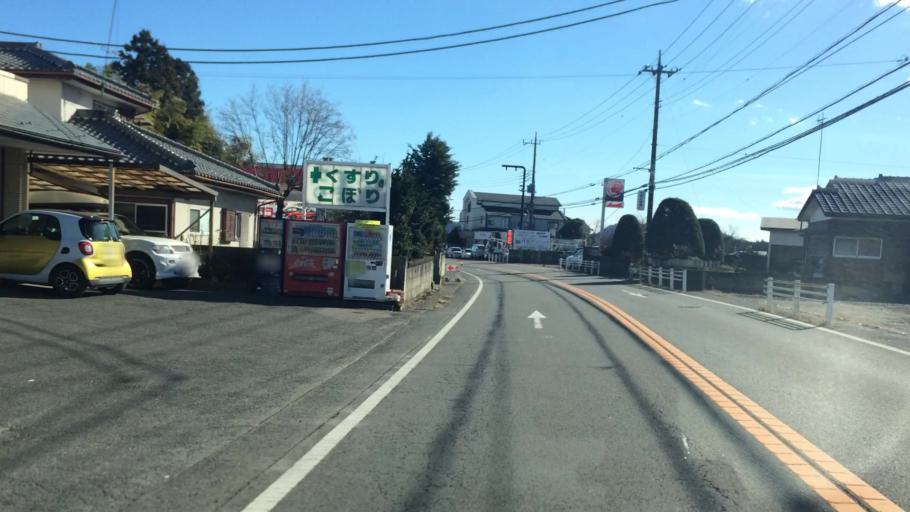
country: JP
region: Tochigi
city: Imaichi
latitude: 36.6927
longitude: 139.7587
